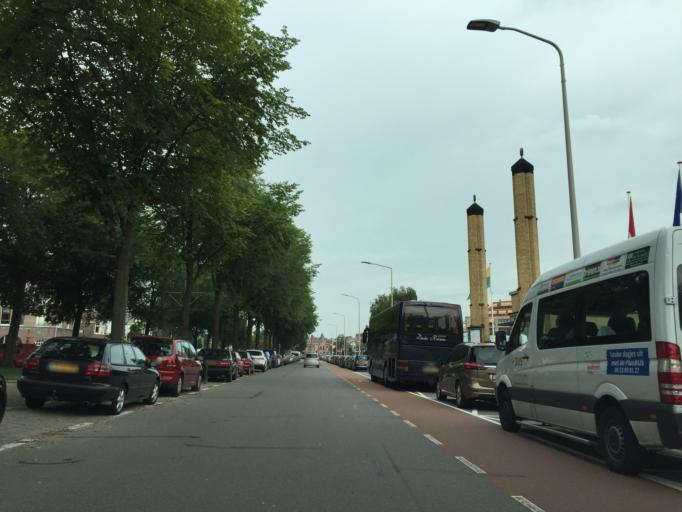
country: NL
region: South Holland
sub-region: Gemeente Den Haag
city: Scheveningen
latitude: 52.0888
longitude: 4.2798
